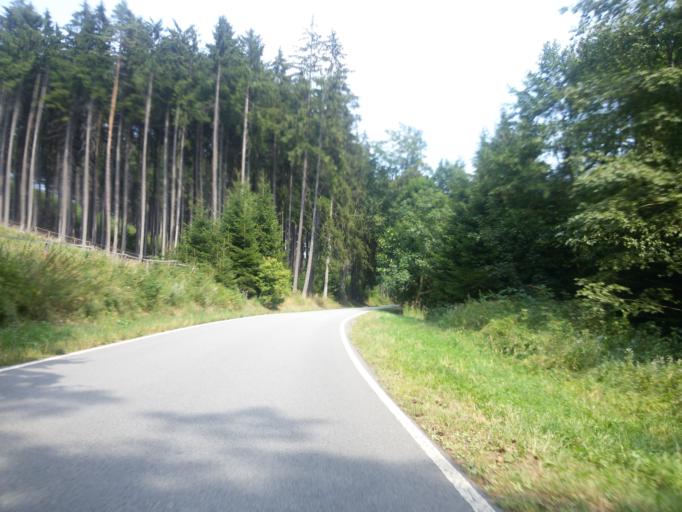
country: CZ
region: South Moravian
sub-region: Okres Brno-Venkov
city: Lomnice
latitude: 49.4610
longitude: 16.4461
